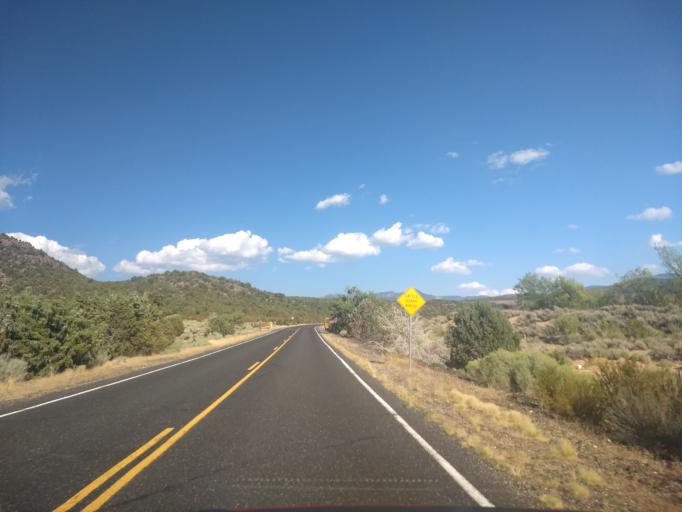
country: US
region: Utah
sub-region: Washington County
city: Enterprise
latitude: 37.4170
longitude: -113.6074
